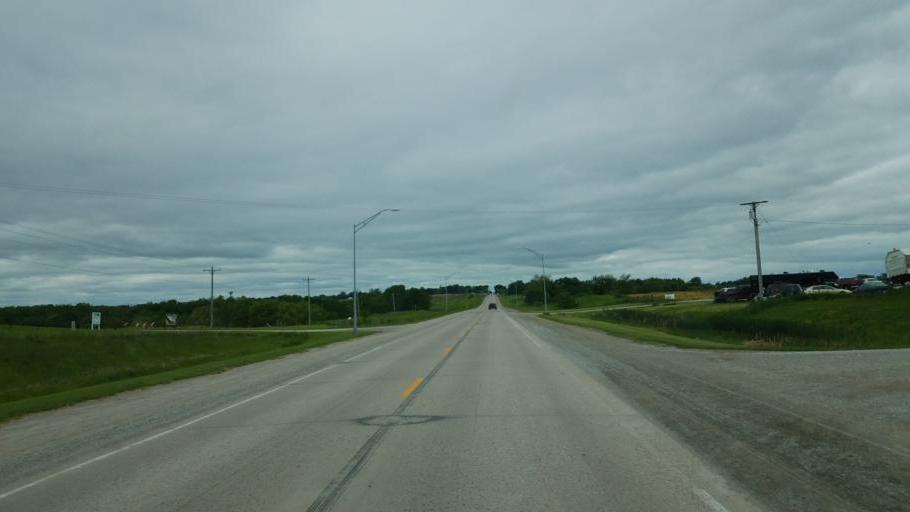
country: US
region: Iowa
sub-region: Decatur County
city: Lamoni
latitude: 40.6236
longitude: -93.9043
